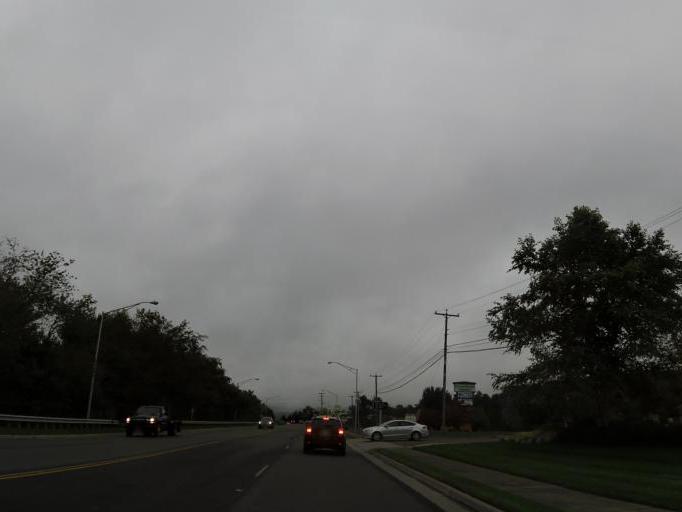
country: US
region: Virginia
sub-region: Wythe County
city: Wytheville
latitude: 36.9573
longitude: -81.0949
